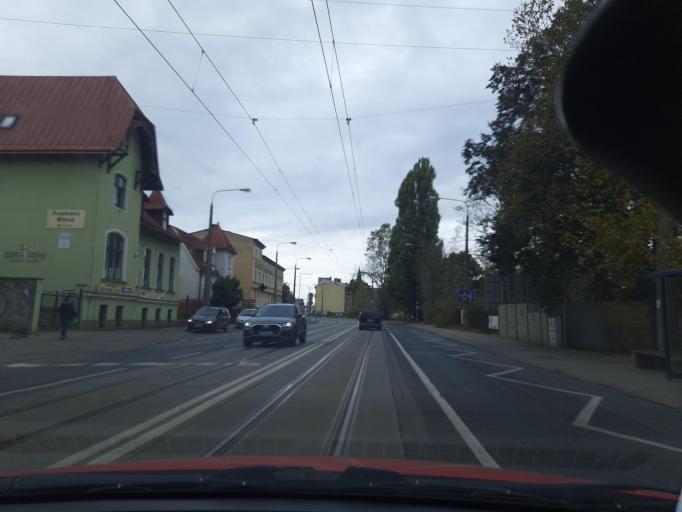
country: PL
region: Kujawsko-Pomorskie
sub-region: Bydgoszcz
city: Bydgoszcz
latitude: 53.1263
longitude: 17.9761
